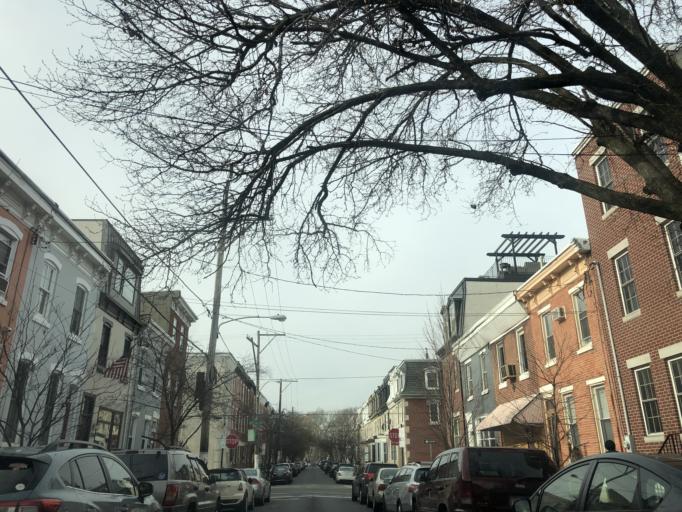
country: US
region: Pennsylvania
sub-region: Philadelphia County
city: Philadelphia
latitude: 39.9425
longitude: -75.1803
